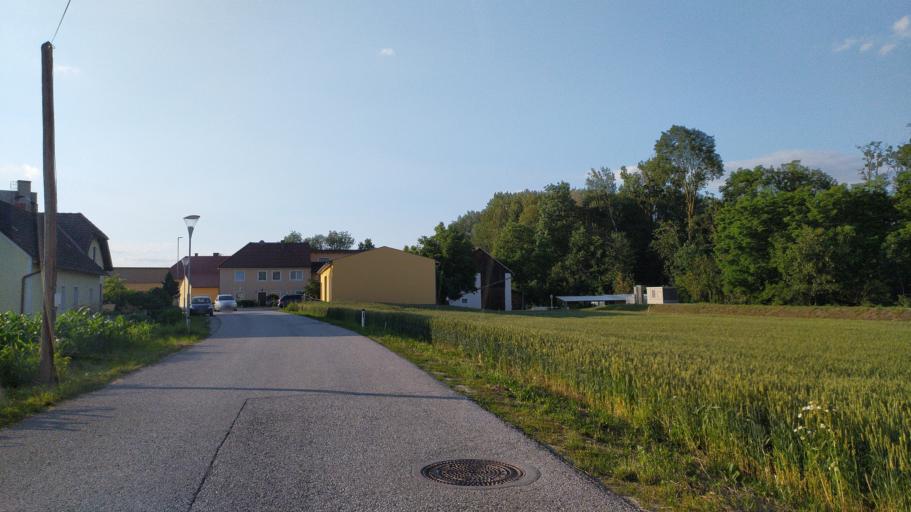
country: AT
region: Lower Austria
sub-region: Politischer Bezirk Amstetten
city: Ennsdorf
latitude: 48.2082
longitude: 14.5711
